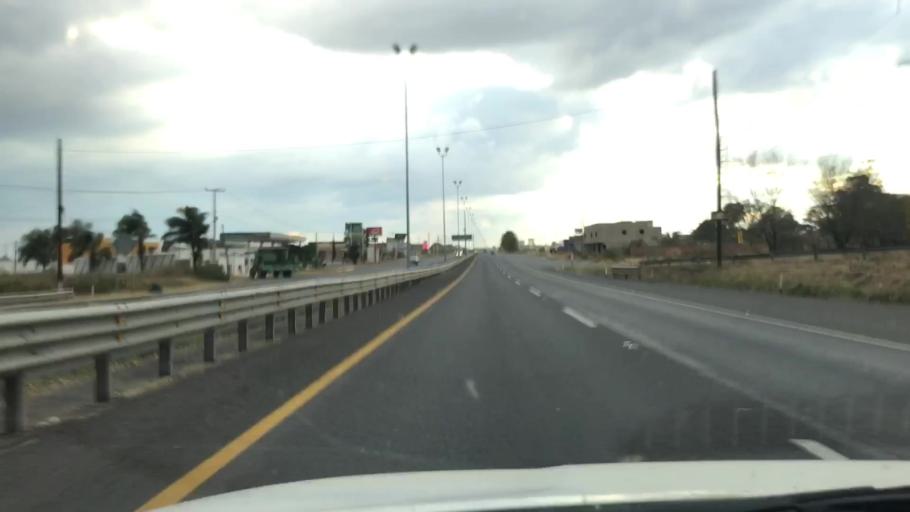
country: MX
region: Guanajuato
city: Penjamo
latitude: 20.4344
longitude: -101.7005
